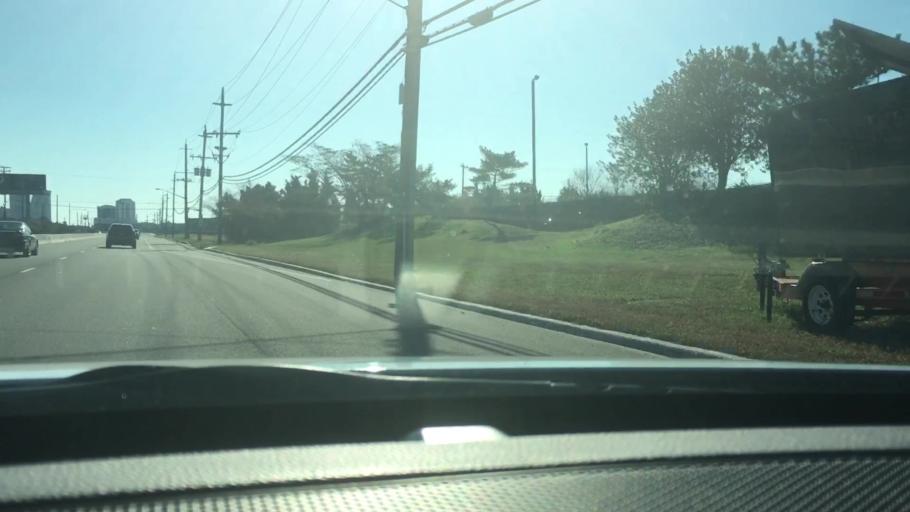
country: US
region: New Jersey
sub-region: Atlantic County
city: Ventnor City
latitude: 39.3651
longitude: -74.4700
